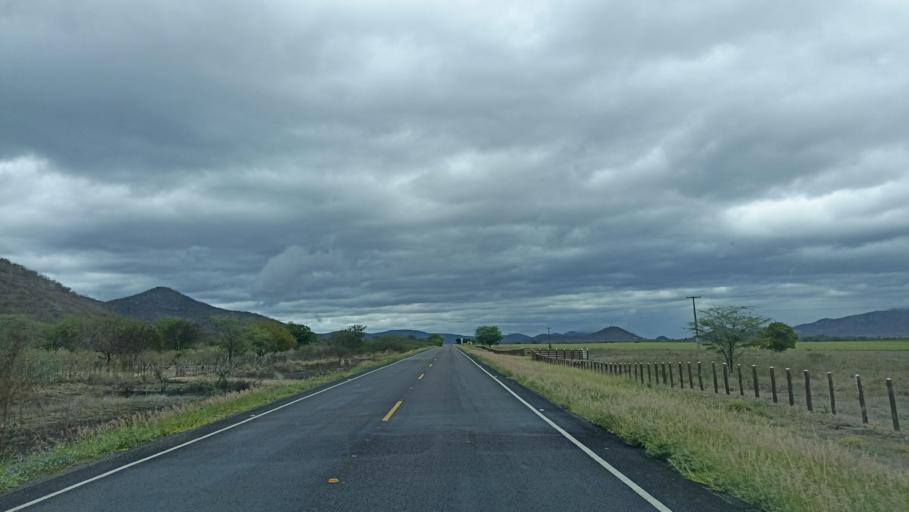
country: BR
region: Bahia
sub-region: Iacu
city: Iacu
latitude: -12.8848
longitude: -40.3928
